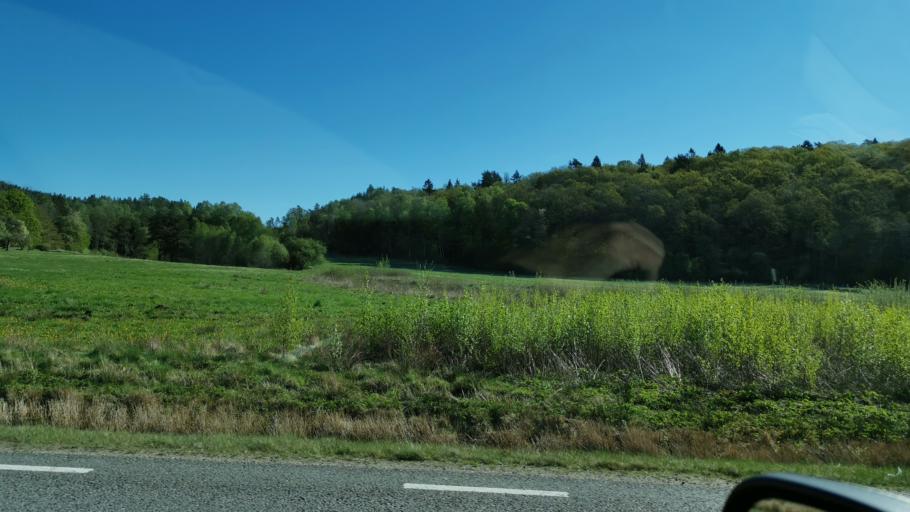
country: SE
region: Vaestra Goetaland
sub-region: Uddevalla Kommun
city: Ljungskile
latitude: 58.2365
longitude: 11.9165
